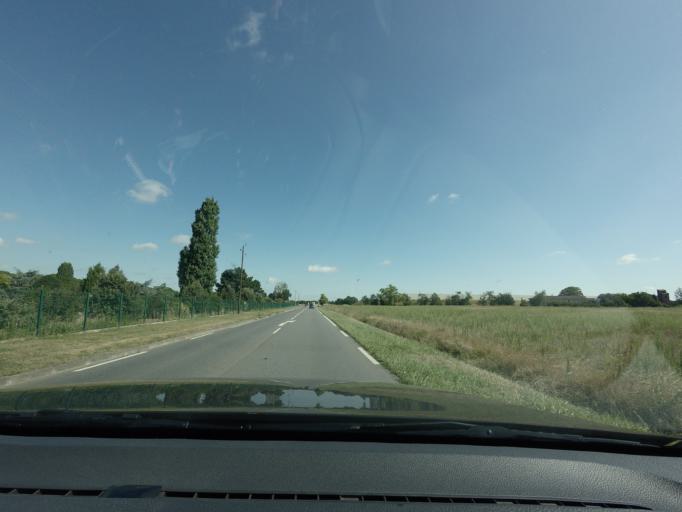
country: FR
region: Midi-Pyrenees
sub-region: Departement de la Haute-Garonne
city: Cornebarrieu
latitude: 43.6344
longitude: 1.3321
